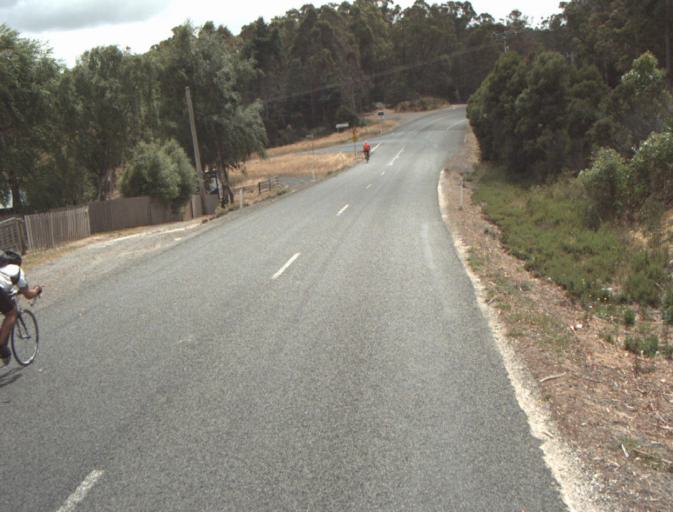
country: AU
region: Tasmania
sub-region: Dorset
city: Bridport
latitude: -41.1638
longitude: 147.2405
